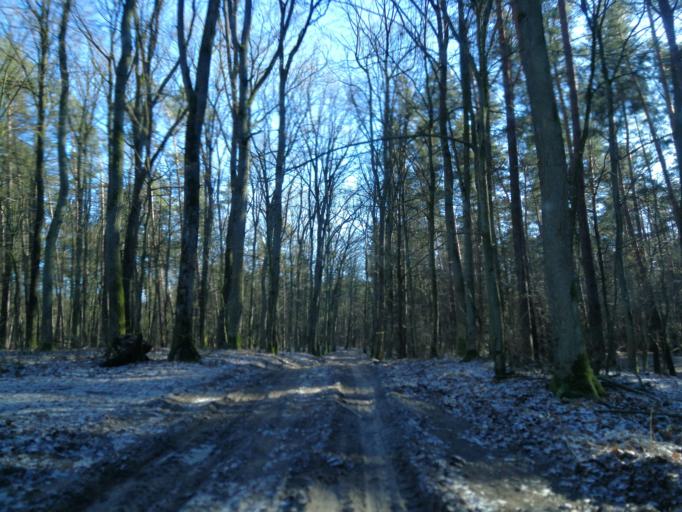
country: PL
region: Kujawsko-Pomorskie
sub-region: Powiat brodnicki
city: Gorzno
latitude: 53.2128
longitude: 19.6768
